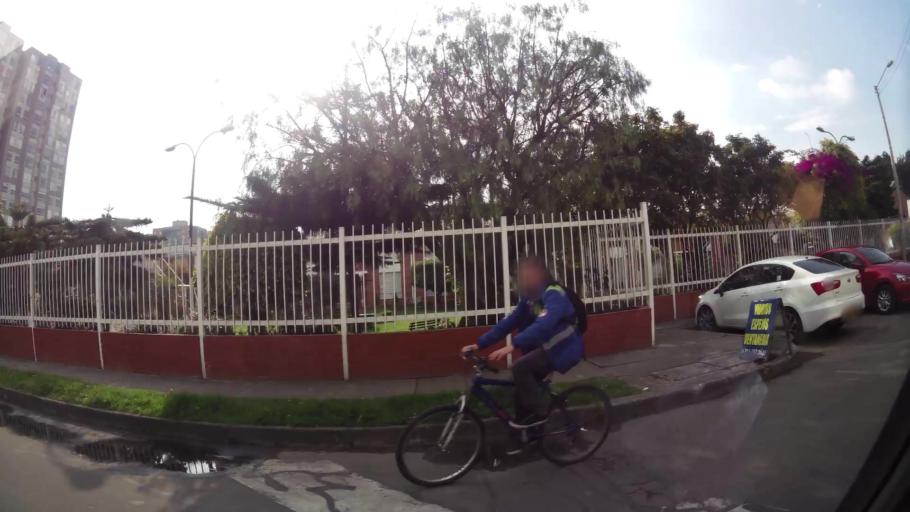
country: CO
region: Bogota D.C.
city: Barrio San Luis
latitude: 4.7286
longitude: -74.0554
